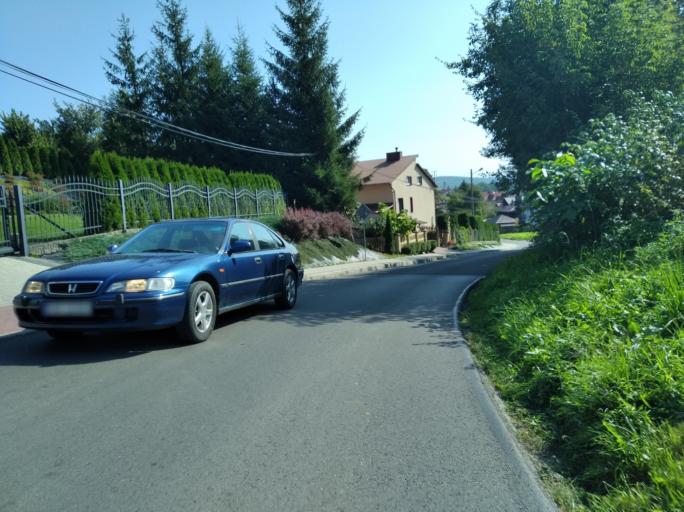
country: PL
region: Subcarpathian Voivodeship
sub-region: Powiat strzyzowski
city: Czudec
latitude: 49.9479
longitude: 21.8377
